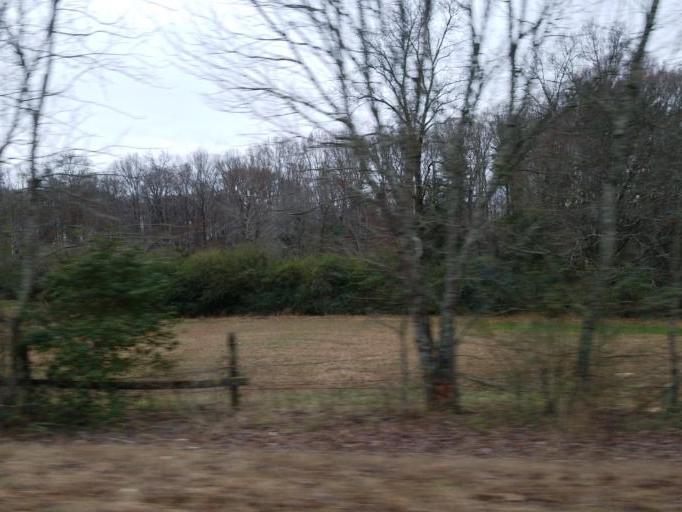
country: US
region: Georgia
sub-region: Dawson County
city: Dawsonville
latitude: 34.4954
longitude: -84.1922
